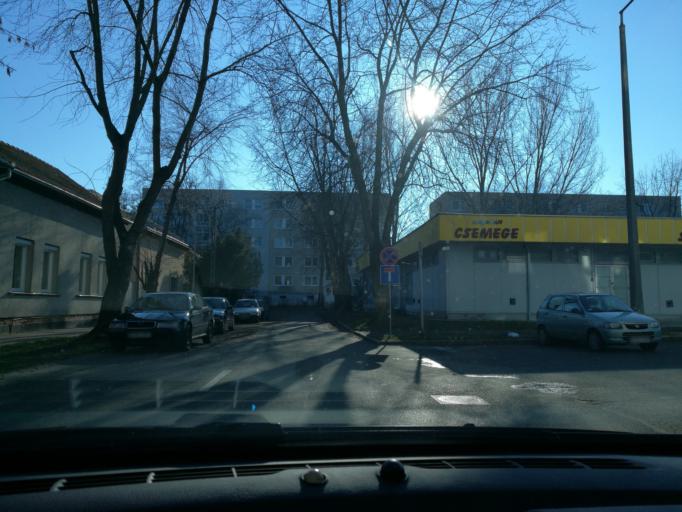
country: HU
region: Szabolcs-Szatmar-Bereg
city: Nyiregyhaza
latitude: 47.9430
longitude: 21.7135
